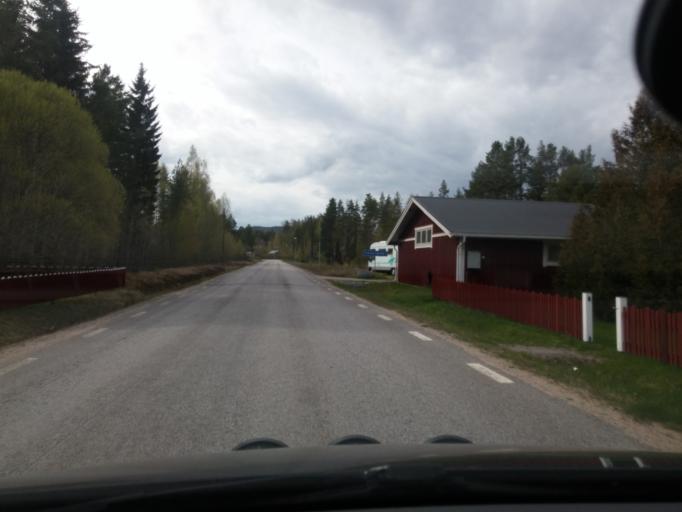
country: SE
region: Gaevleborg
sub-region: Ljusdals Kommun
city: Farila
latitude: 61.7987
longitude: 15.9091
